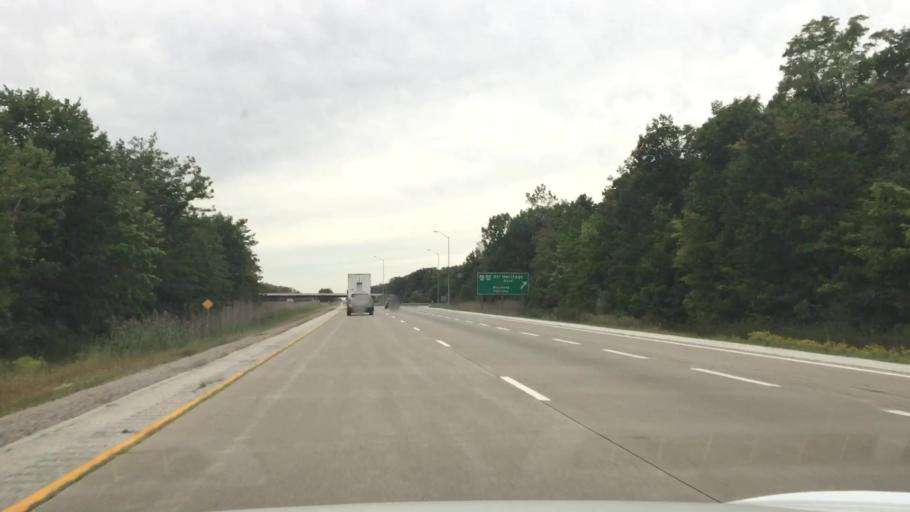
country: CA
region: Ontario
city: Camlachie
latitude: 42.9915
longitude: -82.1099
